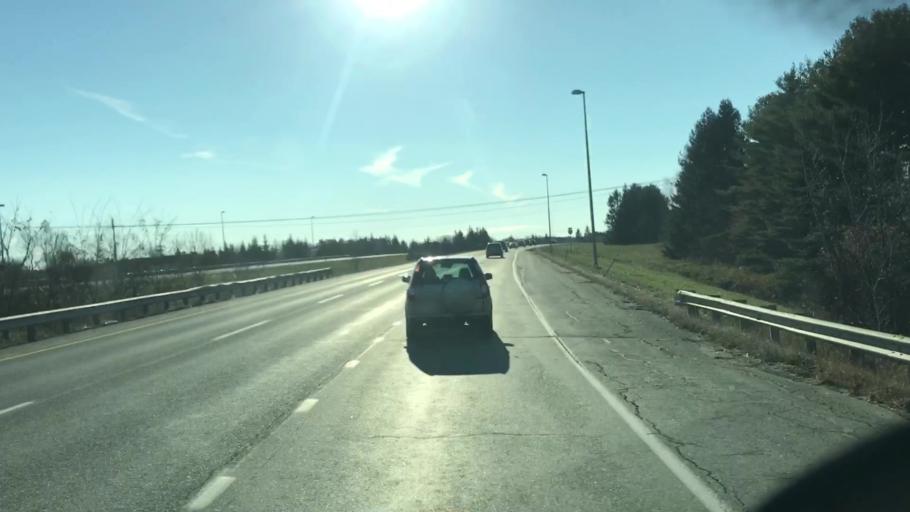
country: US
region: Maine
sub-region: Penobscot County
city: Brewer
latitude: 44.8308
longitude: -68.7437
